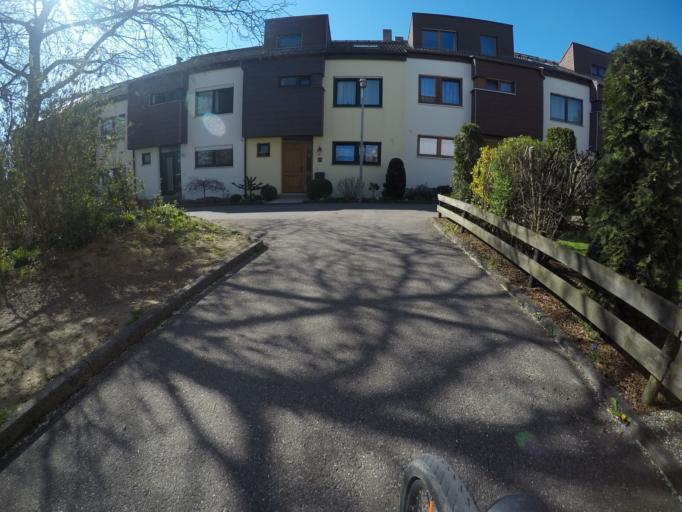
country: DE
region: Baden-Wuerttemberg
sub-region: Regierungsbezirk Stuttgart
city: Filderstadt
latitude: 48.6521
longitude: 9.1919
